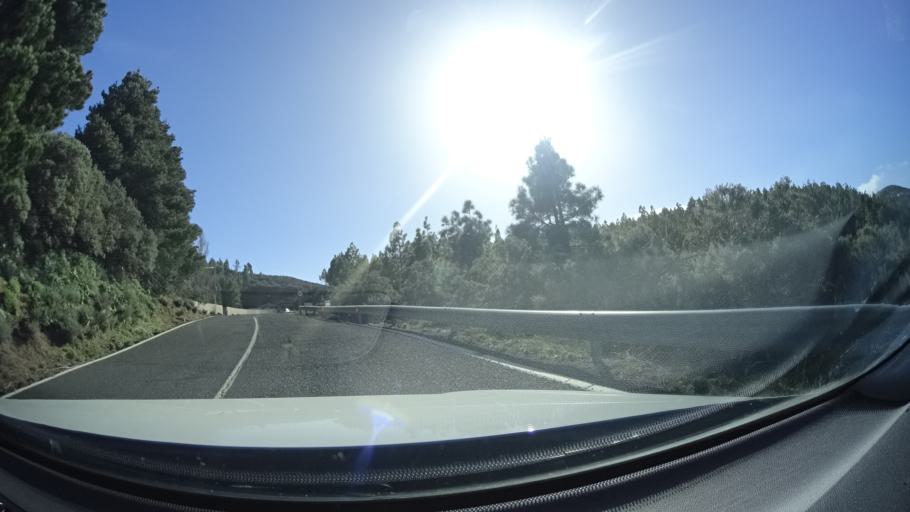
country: ES
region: Canary Islands
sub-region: Provincia de Las Palmas
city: San Bartolome
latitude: 27.9646
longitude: -15.5505
